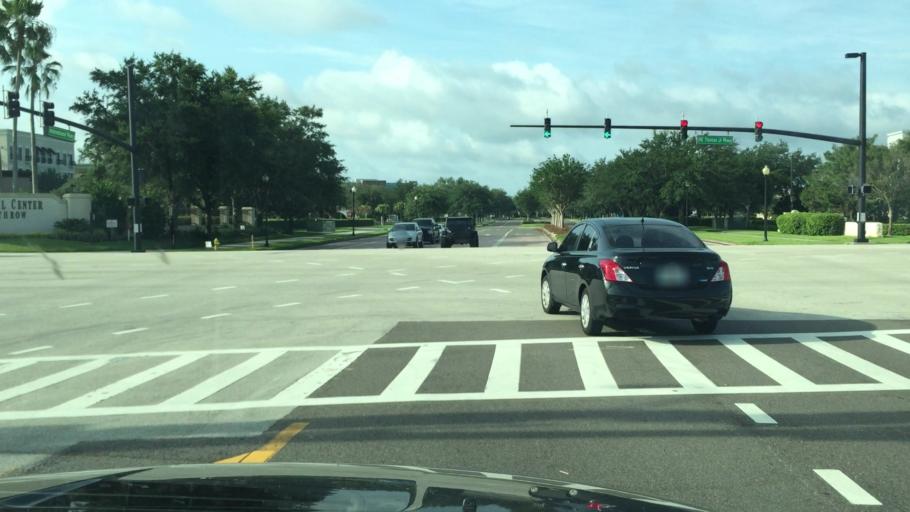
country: US
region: Florida
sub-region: Seminole County
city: Heathrow
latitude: 28.7867
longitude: -81.3580
